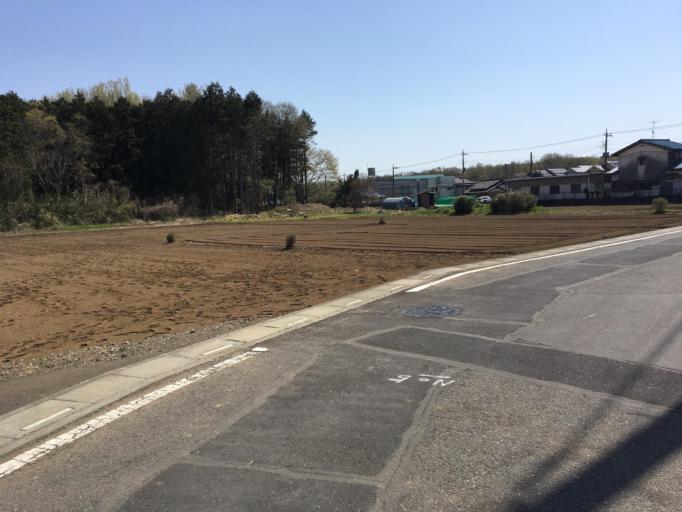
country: JP
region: Saitama
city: Morohongo
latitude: 35.9539
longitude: 139.3423
